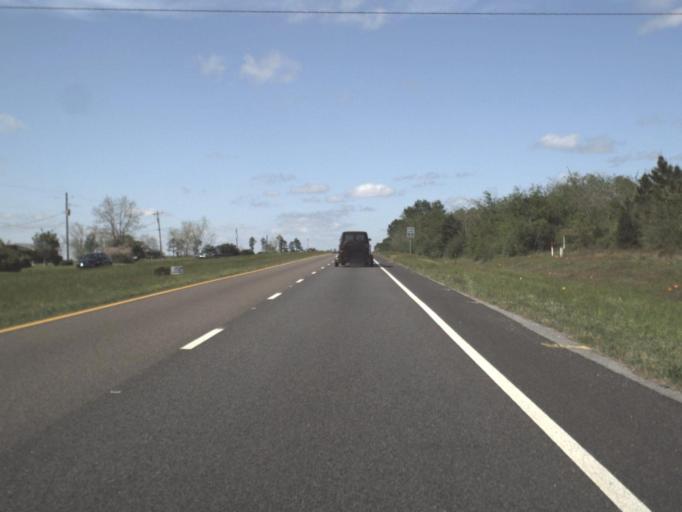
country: US
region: Florida
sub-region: Escambia County
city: Molino
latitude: 30.7185
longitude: -87.3496
